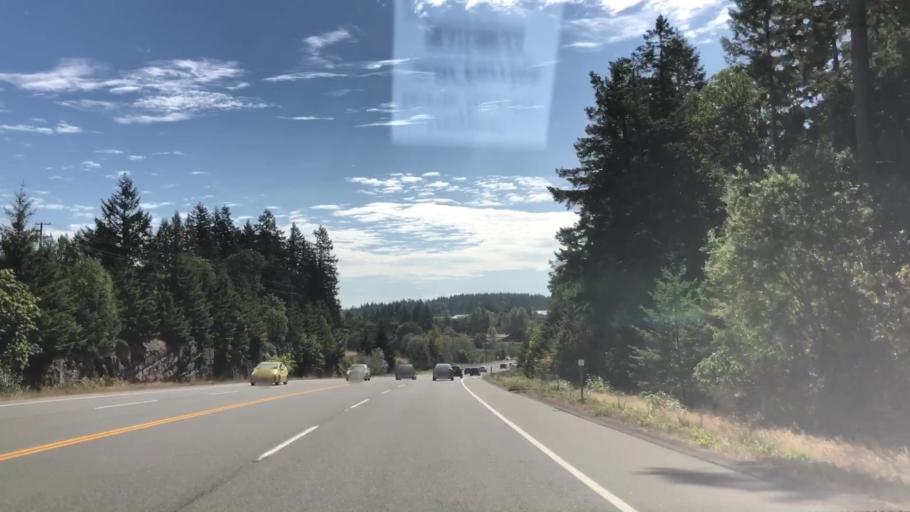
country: CA
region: British Columbia
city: Nanaimo
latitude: 49.1322
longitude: -123.8674
